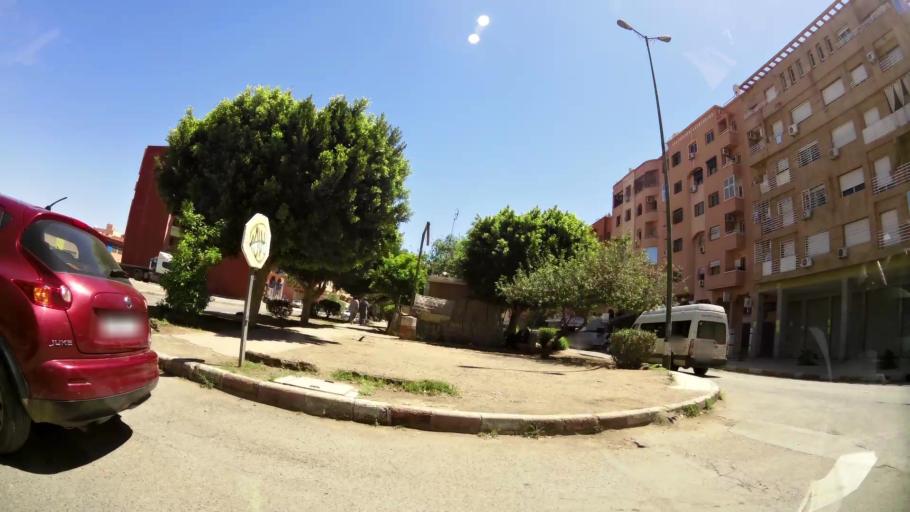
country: MA
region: Marrakech-Tensift-Al Haouz
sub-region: Marrakech
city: Marrakesh
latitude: 31.6342
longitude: -8.0608
